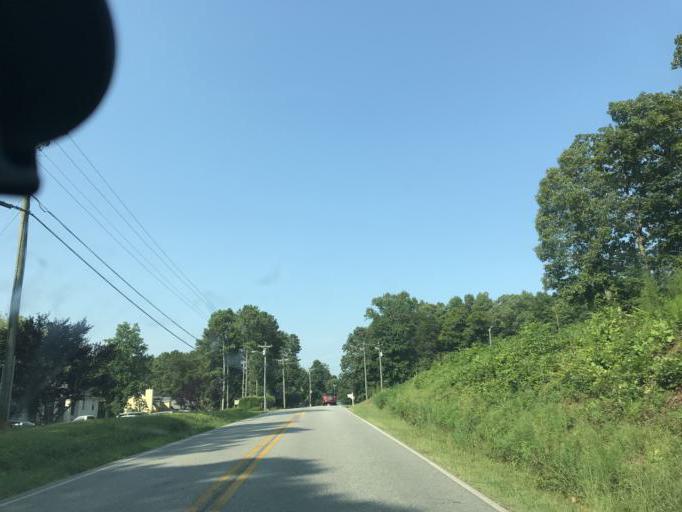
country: US
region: Georgia
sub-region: Forsyth County
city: Cumming
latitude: 34.2348
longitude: -84.1056
